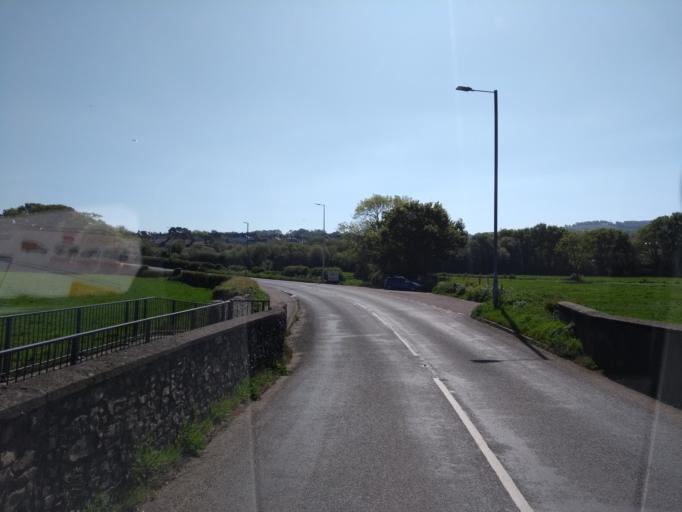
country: GB
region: England
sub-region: Devon
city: Axminster
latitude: 50.7791
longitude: -3.0082
